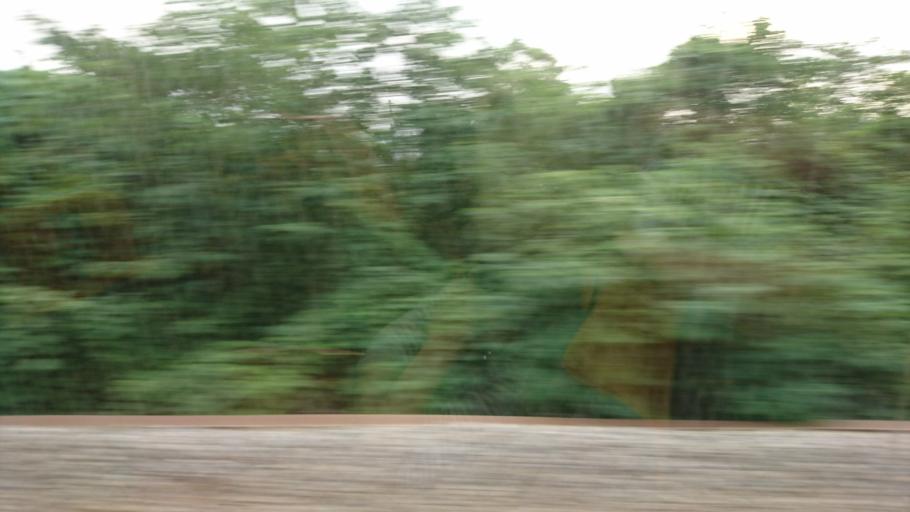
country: TW
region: Taiwan
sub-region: Hsinchu
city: Zhubei
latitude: 24.8576
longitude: 121.0018
